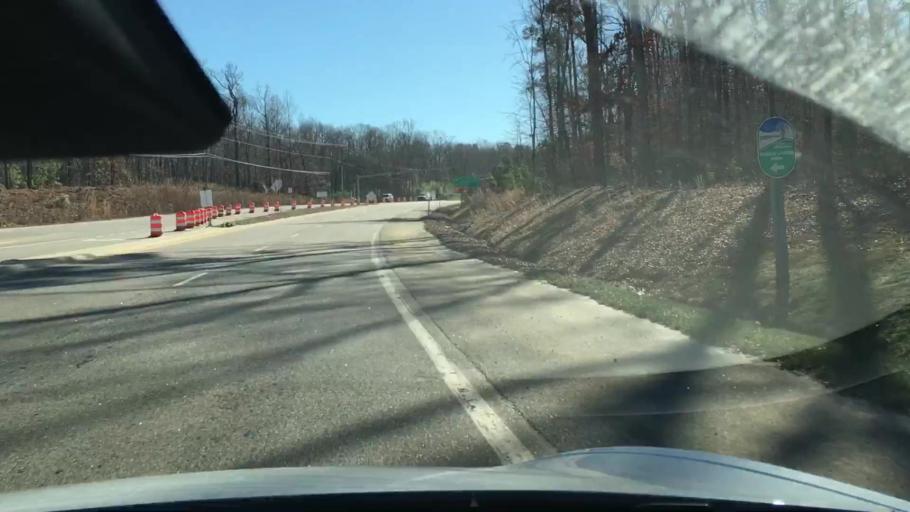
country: US
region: Virginia
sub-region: Chesterfield County
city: Bon Air
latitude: 37.5489
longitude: -77.6545
